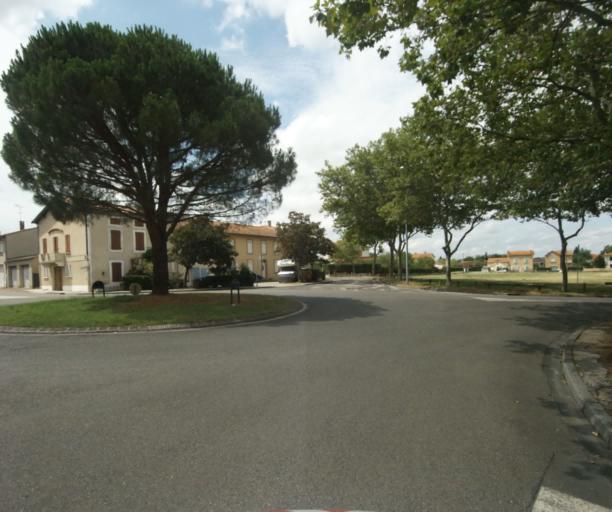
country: FR
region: Midi-Pyrenees
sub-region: Departement de la Haute-Garonne
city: Revel
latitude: 43.4537
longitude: 2.0013
